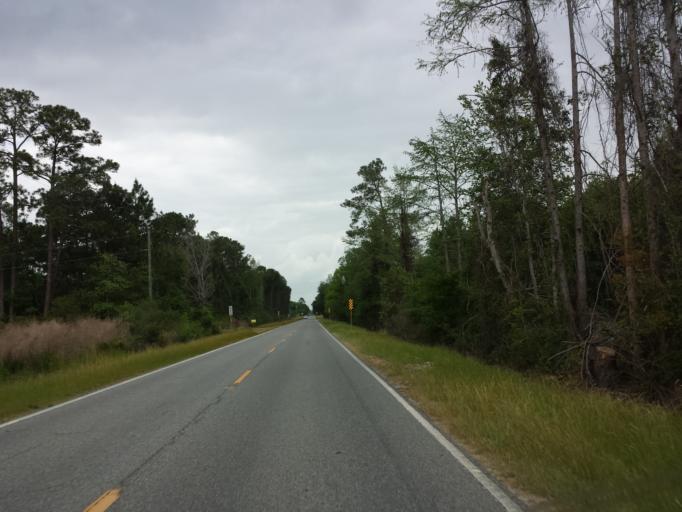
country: US
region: Georgia
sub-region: Tift County
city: Unionville
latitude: 31.3220
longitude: -83.4771
